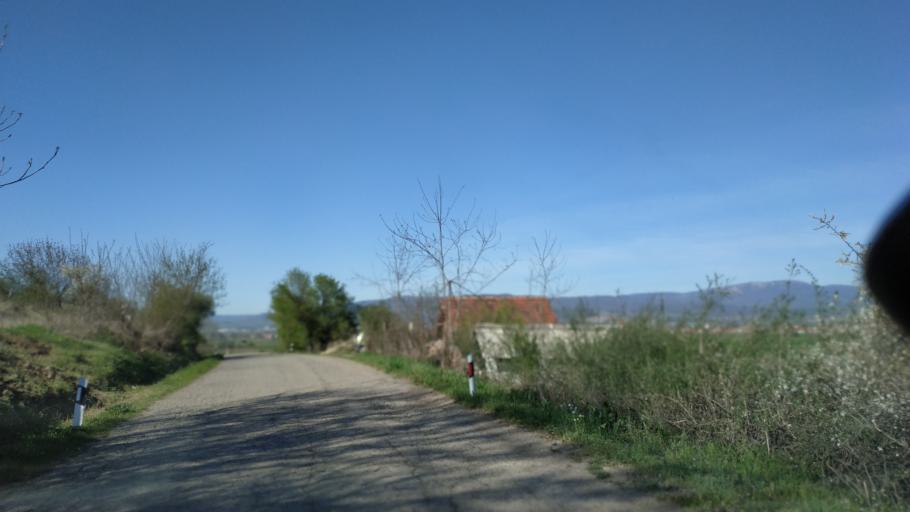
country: RS
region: Central Serbia
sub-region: Nisavski Okrug
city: Aleksinac
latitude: 43.4967
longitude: 21.6748
